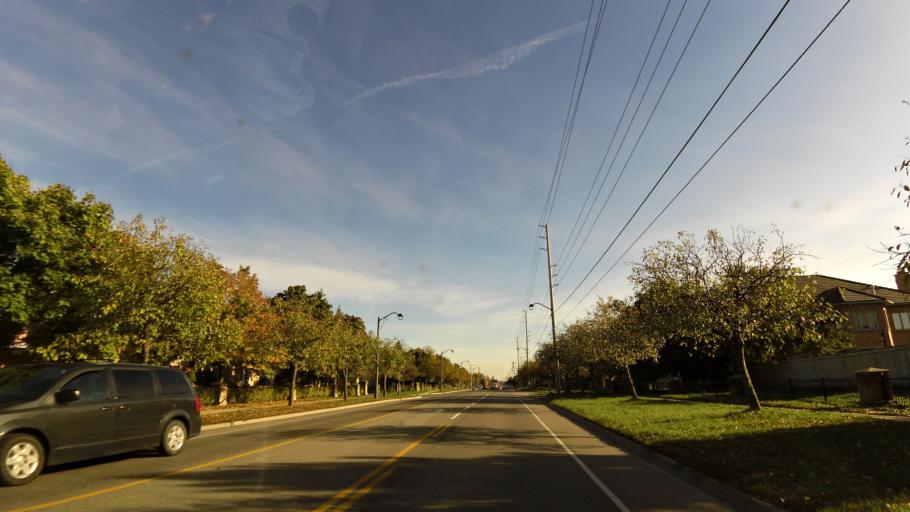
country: CA
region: Ontario
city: Mississauga
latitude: 43.5701
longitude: -79.6981
